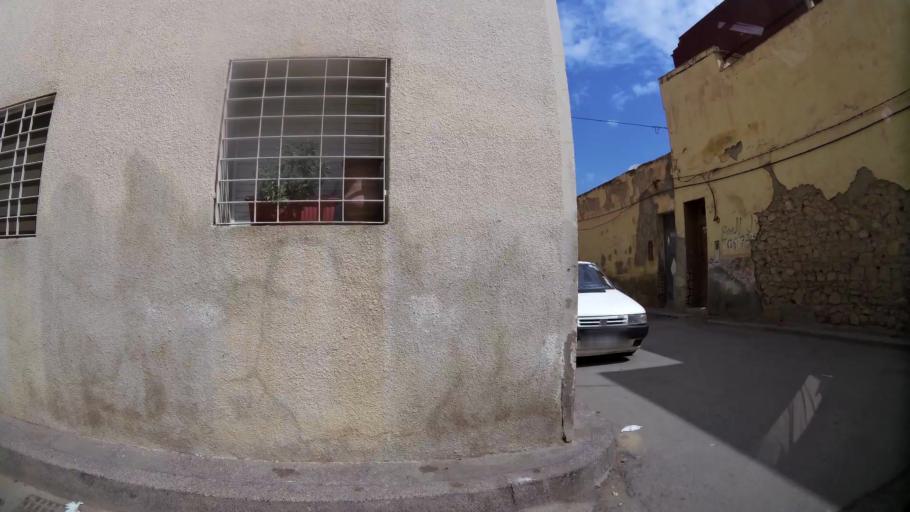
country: MA
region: Oriental
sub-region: Oujda-Angad
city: Oujda
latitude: 34.6826
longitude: -1.9060
